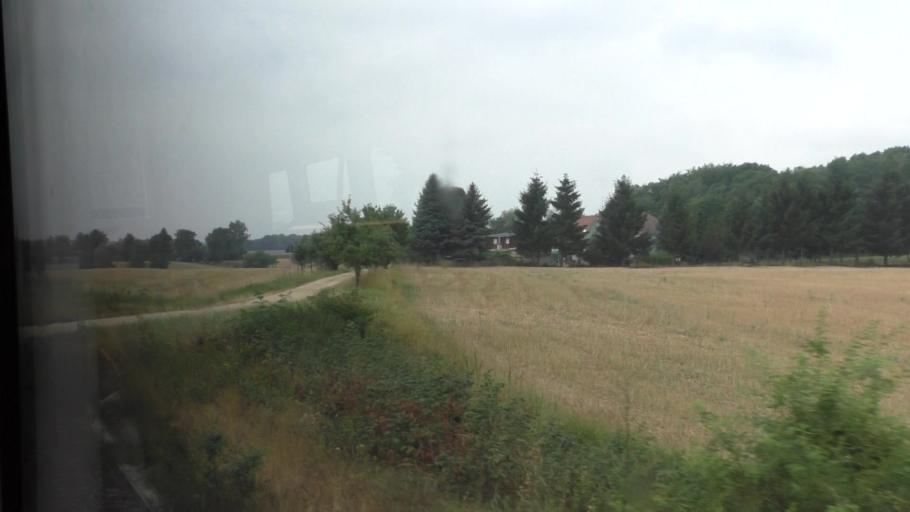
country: DE
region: Saxony
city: Hirschfelde
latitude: 50.9172
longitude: 14.8522
